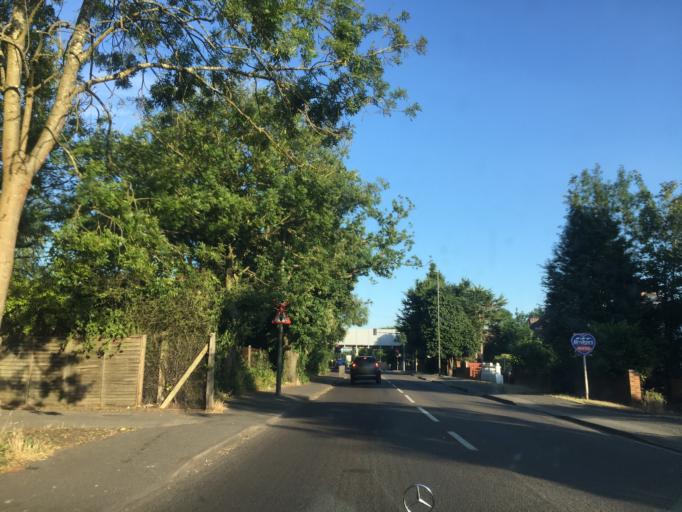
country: GB
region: England
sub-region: Surrey
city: Frimley
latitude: 51.3202
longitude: -0.7514
